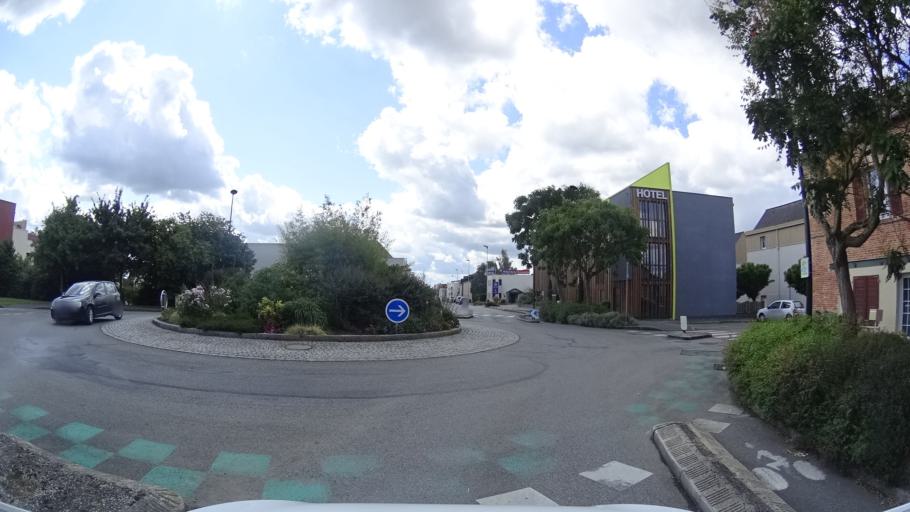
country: FR
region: Brittany
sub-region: Departement d'Ille-et-Vilaine
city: Chartres-de-Bretagne
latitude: 48.0353
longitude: -1.7125
